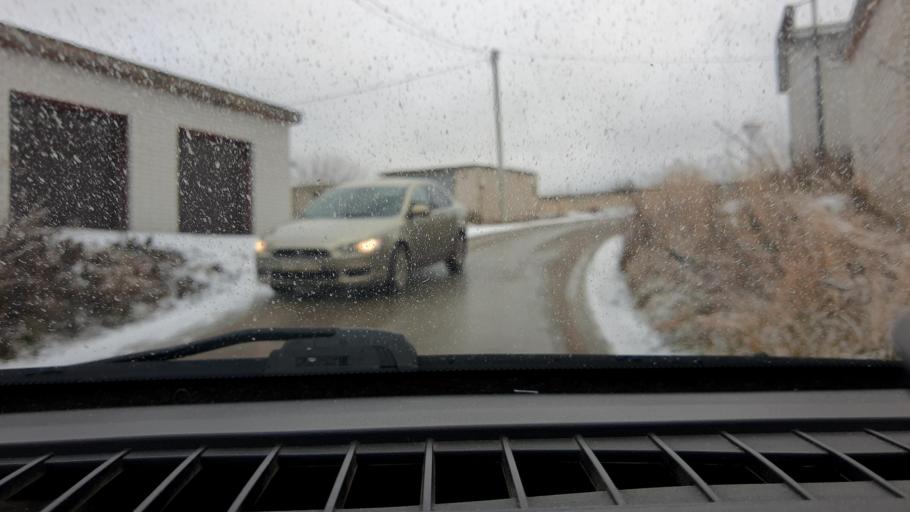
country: RU
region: Nizjnij Novgorod
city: Taremskoye
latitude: 55.9410
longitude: 43.0624
